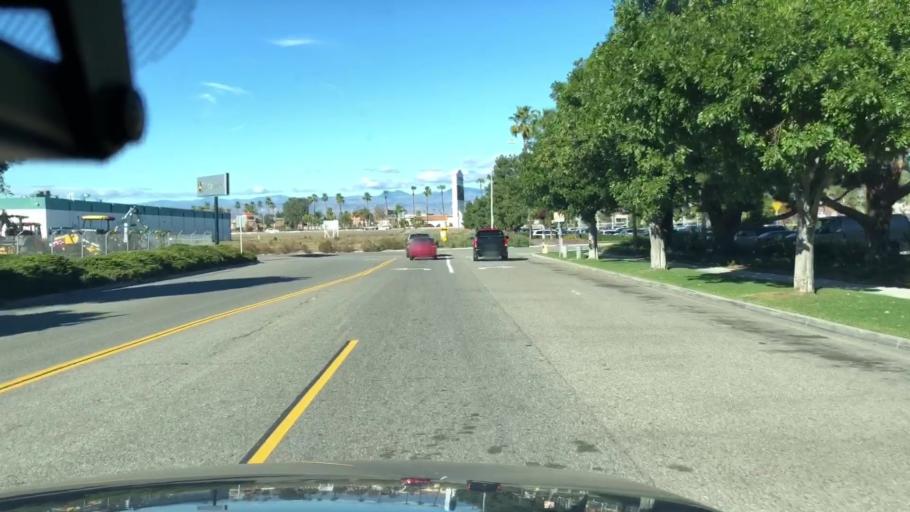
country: US
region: California
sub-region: Ventura County
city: El Rio
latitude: 34.2215
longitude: -119.1539
